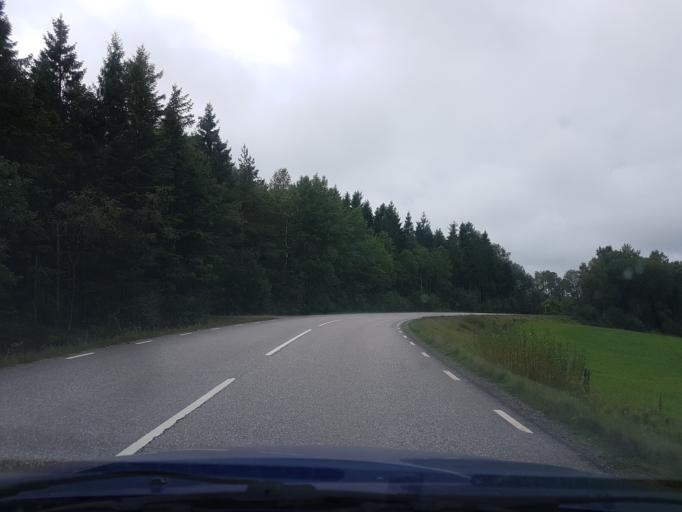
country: SE
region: Vaestra Goetaland
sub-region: Ale Kommun
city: Alvangen
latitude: 57.9450
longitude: 12.1693
